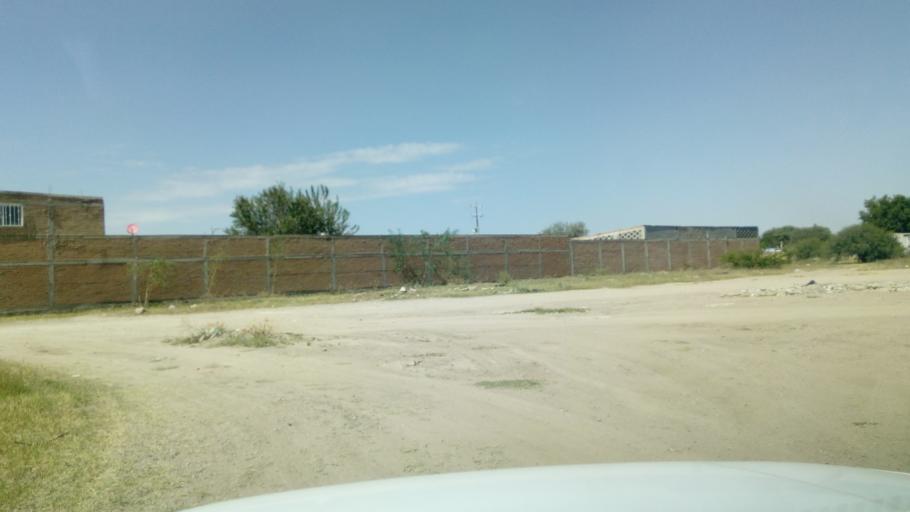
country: MX
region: Durango
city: Victoria de Durango
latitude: 23.9895
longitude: -104.6829
